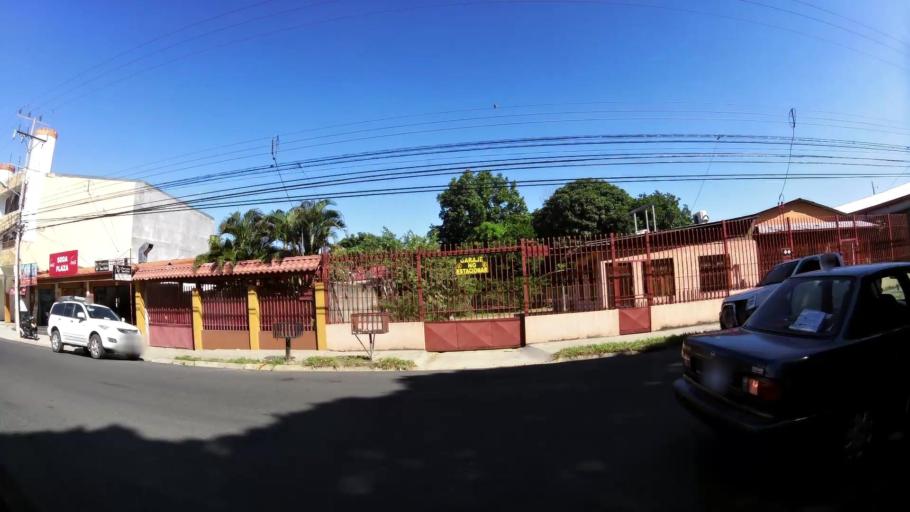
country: CR
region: Guanacaste
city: Liberia
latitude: 10.6352
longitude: -85.4326
